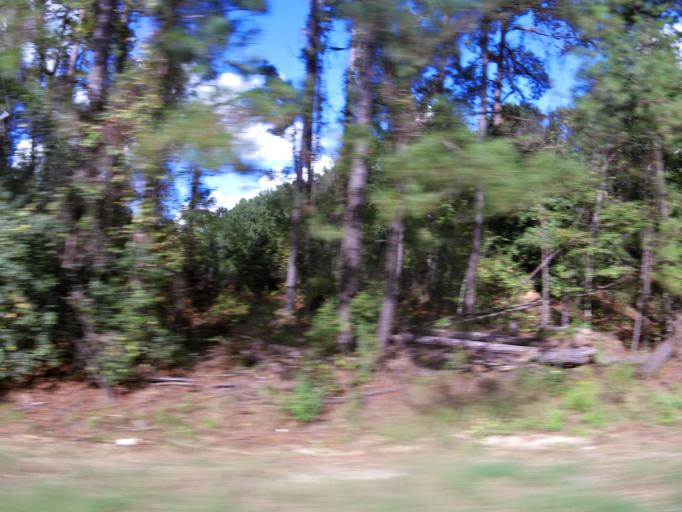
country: US
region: Georgia
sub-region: Echols County
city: Statenville
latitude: 30.7701
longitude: -83.1382
